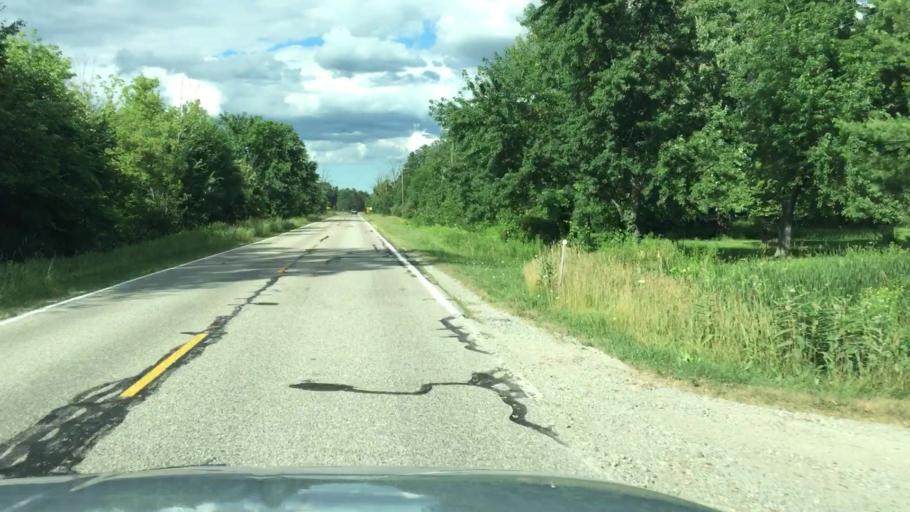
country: US
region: Michigan
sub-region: Saint Clair County
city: Capac
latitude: 43.1081
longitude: -82.9051
